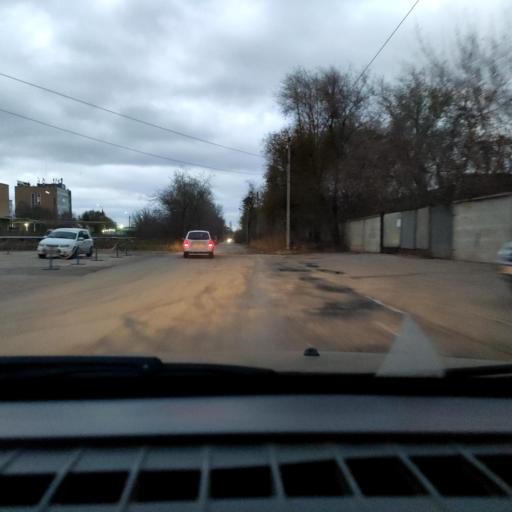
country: RU
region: Samara
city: Tol'yatti
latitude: 53.5627
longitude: 49.3142
